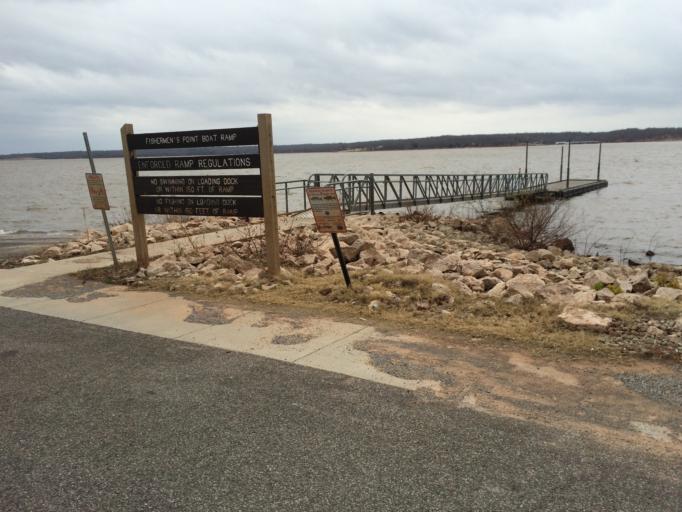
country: US
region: Oklahoma
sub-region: Pottawatomie County
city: Pink
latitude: 35.2291
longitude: -97.2472
